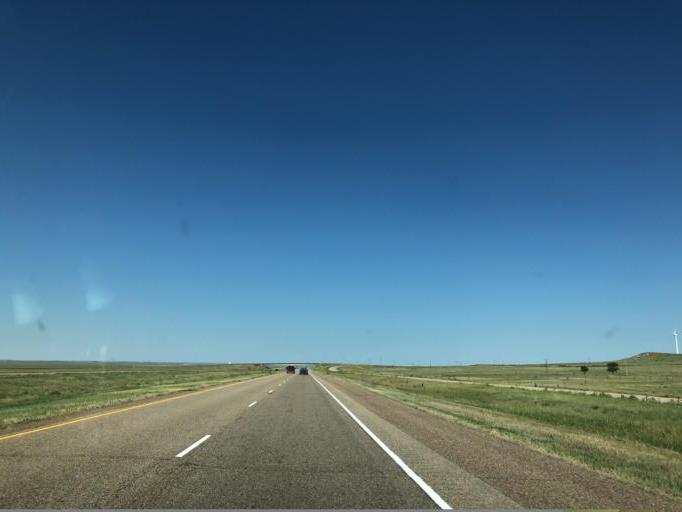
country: US
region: Colorado
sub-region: Lincoln County
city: Hugo
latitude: 39.2671
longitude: -103.5370
